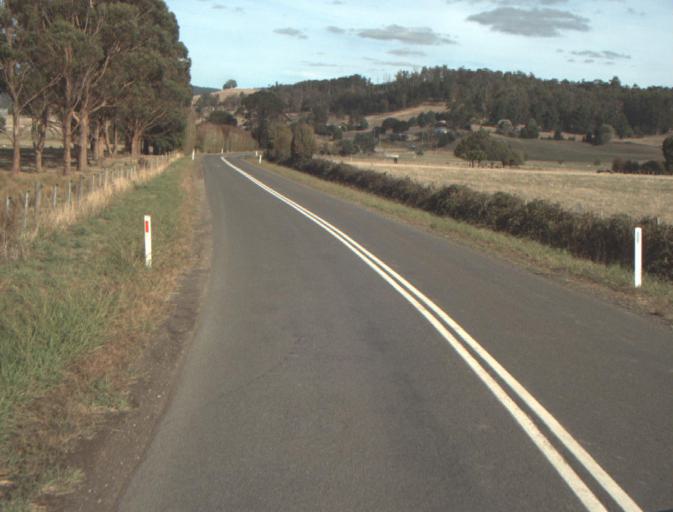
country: AU
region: Tasmania
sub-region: Launceston
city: Mayfield
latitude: -41.2290
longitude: 147.1230
